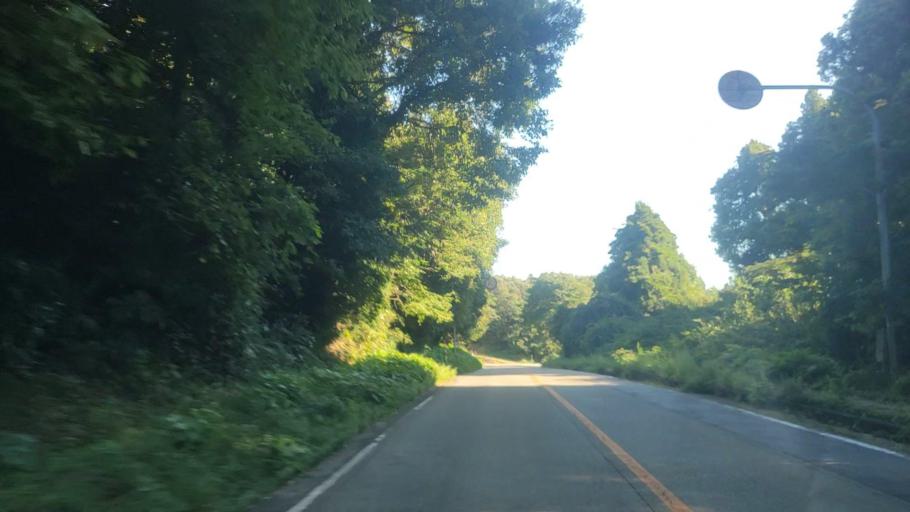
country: JP
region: Ishikawa
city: Nanao
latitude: 37.1033
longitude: 136.9482
